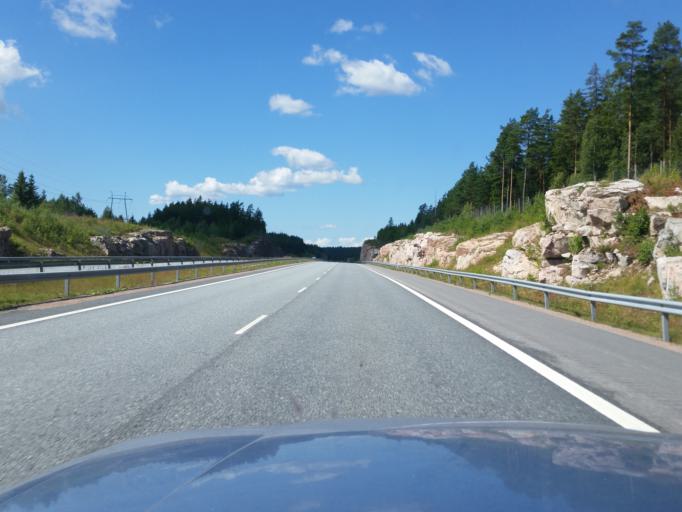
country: FI
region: Varsinais-Suomi
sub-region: Salo
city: Kiikala
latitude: 60.3922
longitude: 23.5536
